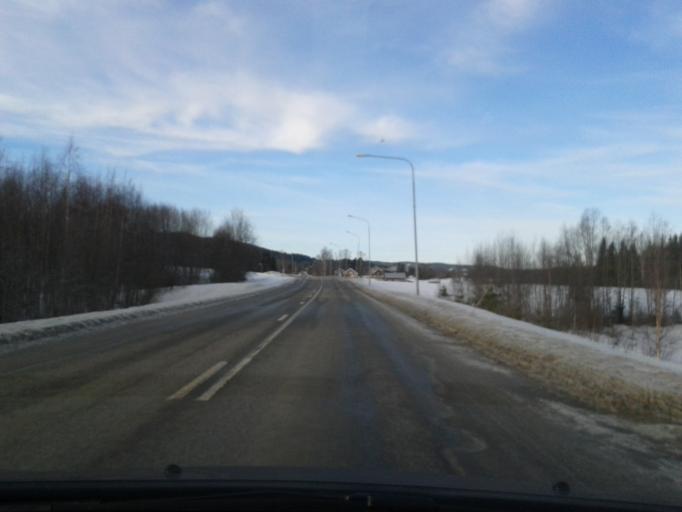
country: SE
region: Vaesternorrland
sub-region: OErnskoeldsviks Kommun
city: Bredbyn
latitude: 63.4784
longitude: 18.0933
